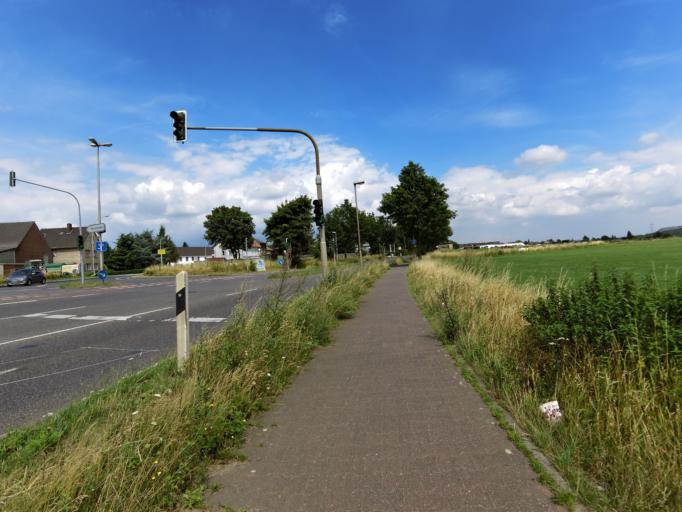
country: NL
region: Limburg
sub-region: Gemeente Kerkrade
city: Kerkrade
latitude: 50.8443
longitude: 6.0742
